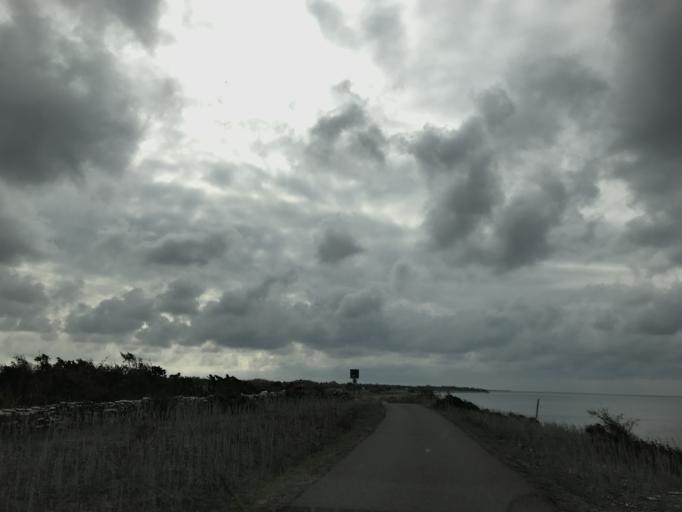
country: SE
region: Kalmar
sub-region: Borgholms Kommun
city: Borgholm
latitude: 57.0566
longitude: 16.8373
